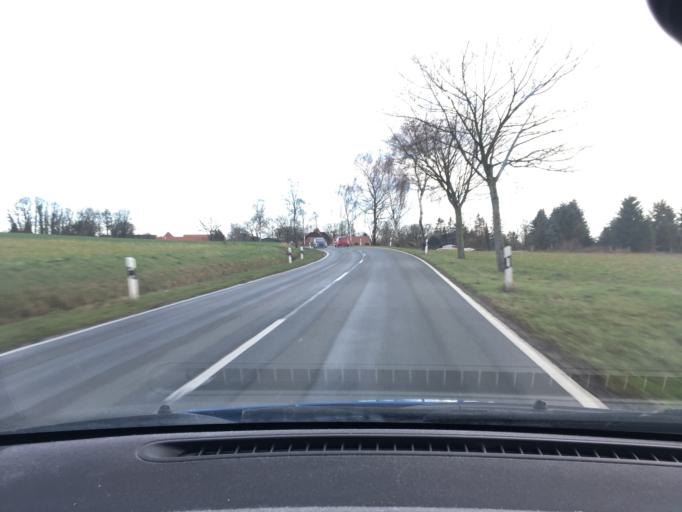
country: DE
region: Lower Saxony
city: Egestorf
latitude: 53.2151
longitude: 10.0284
